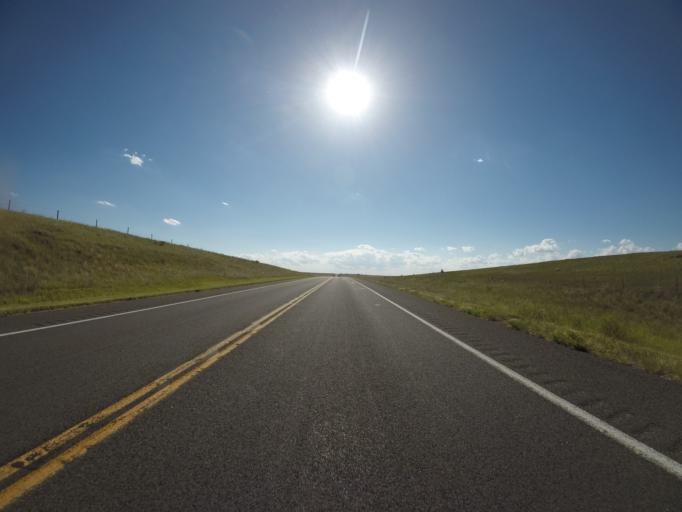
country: US
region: Colorado
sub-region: Morgan County
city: Brush
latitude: 40.6110
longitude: -103.5684
